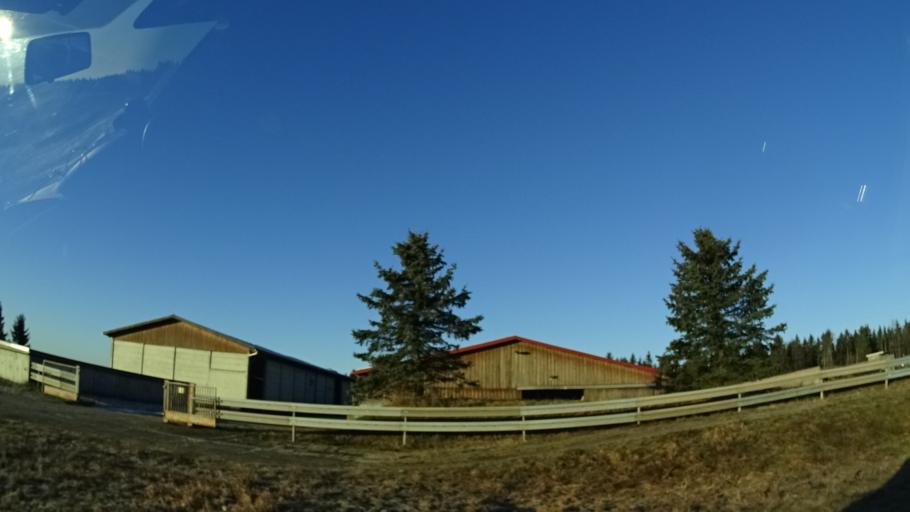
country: DE
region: Thuringia
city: Judenbach
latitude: 50.4088
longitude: 11.2286
